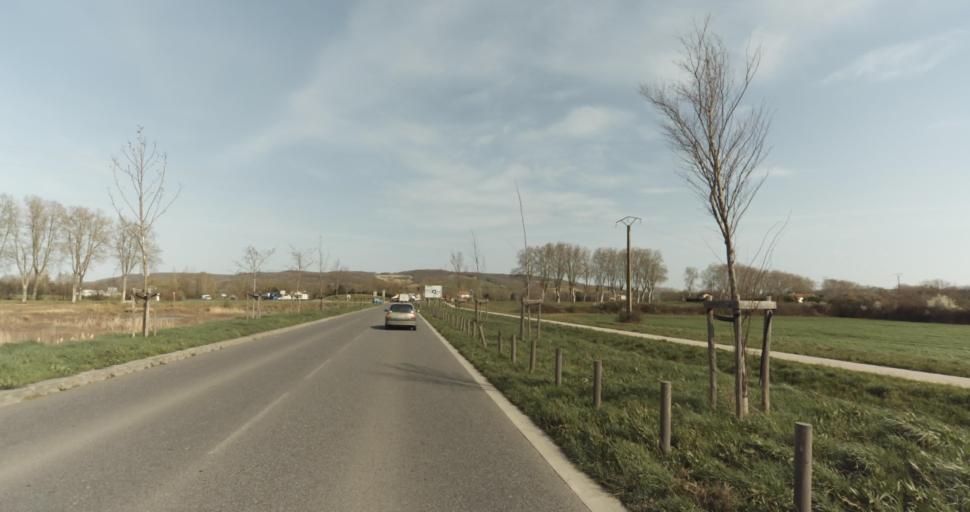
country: FR
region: Midi-Pyrenees
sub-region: Departement de la Haute-Garonne
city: Buzet-sur-Tarn
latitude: 43.7694
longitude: 1.6560
